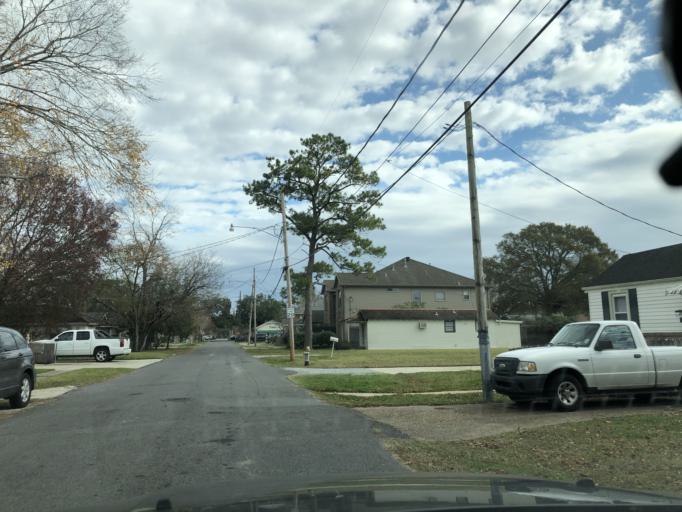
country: US
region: Louisiana
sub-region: Jefferson Parish
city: Metairie Terrace
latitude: 29.9793
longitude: -90.1686
